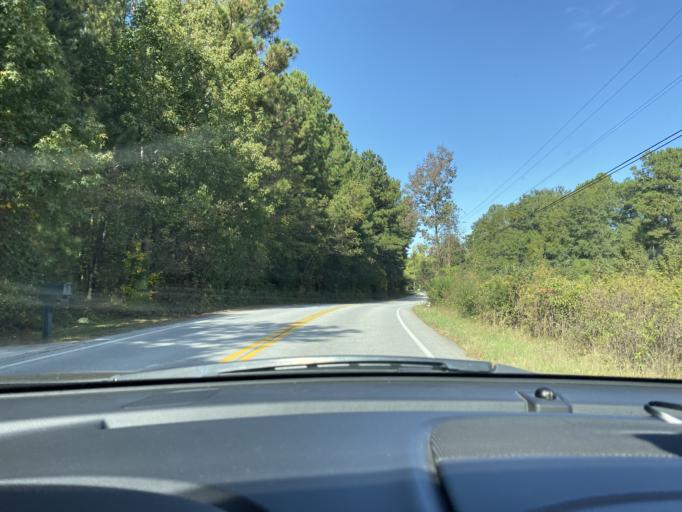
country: US
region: Georgia
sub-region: Walton County
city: Loganville
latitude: 33.8719
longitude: -83.9107
